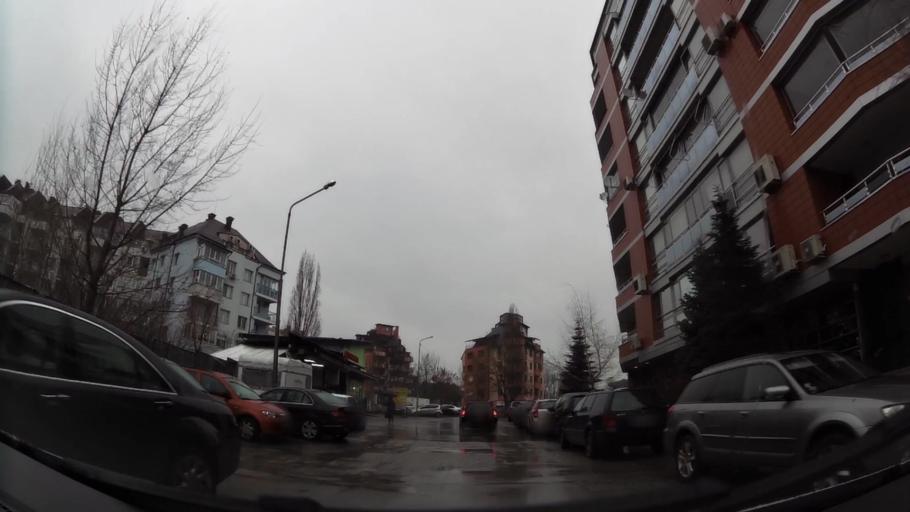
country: BG
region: Sofia-Capital
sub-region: Stolichna Obshtina
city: Sofia
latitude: 42.6440
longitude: 23.3370
